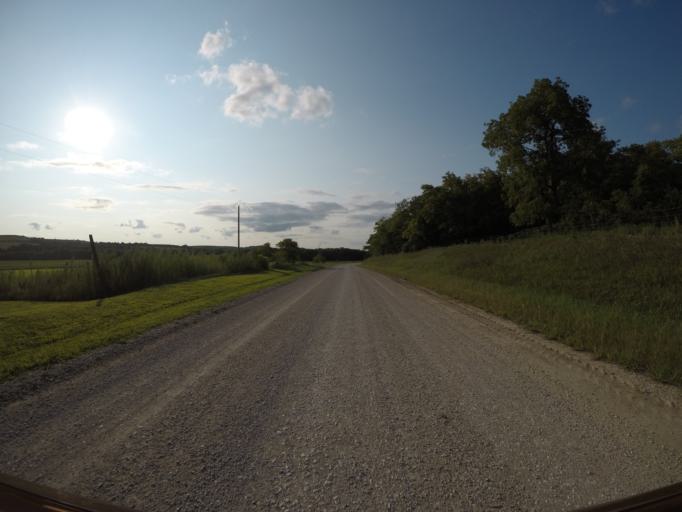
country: US
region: Kansas
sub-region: Wabaunsee County
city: Alma
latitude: 38.9455
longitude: -96.2396
